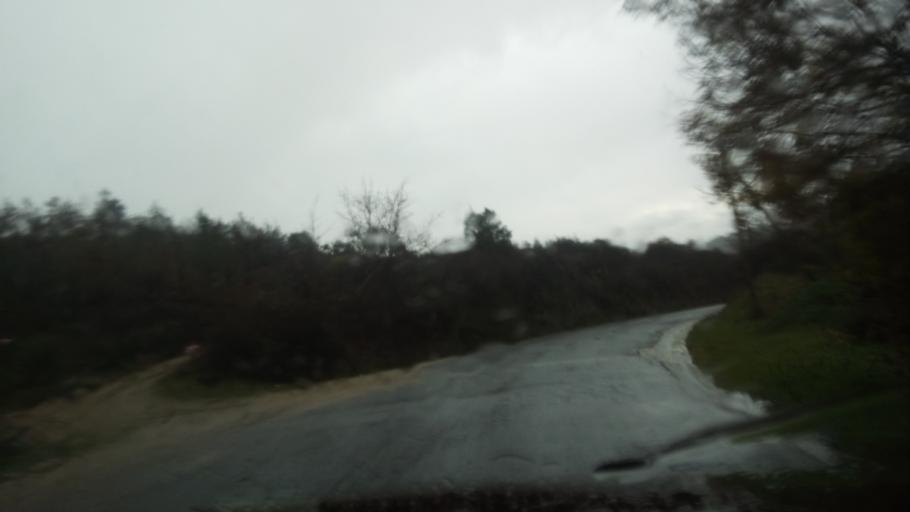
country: PT
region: Guarda
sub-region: Fornos de Algodres
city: Fornos de Algodres
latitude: 40.6226
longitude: -7.4753
